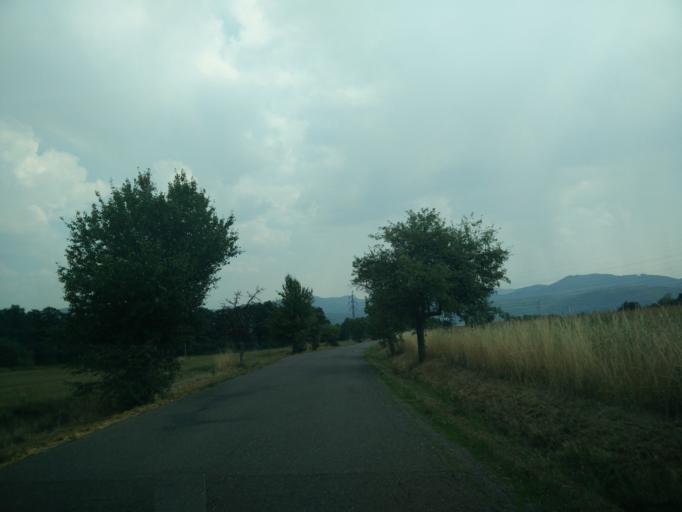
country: SK
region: Banskobystricky
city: Zarnovica
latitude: 48.5609
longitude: 18.7544
